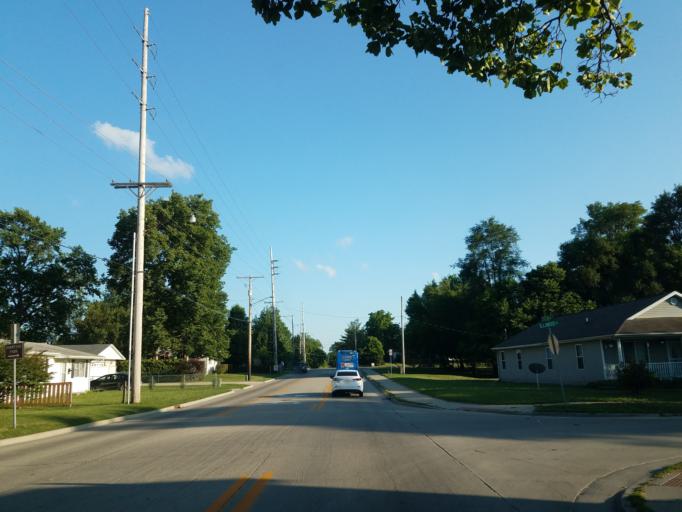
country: US
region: Illinois
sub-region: McLean County
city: Bloomington
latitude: 40.4755
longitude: -89.0162
